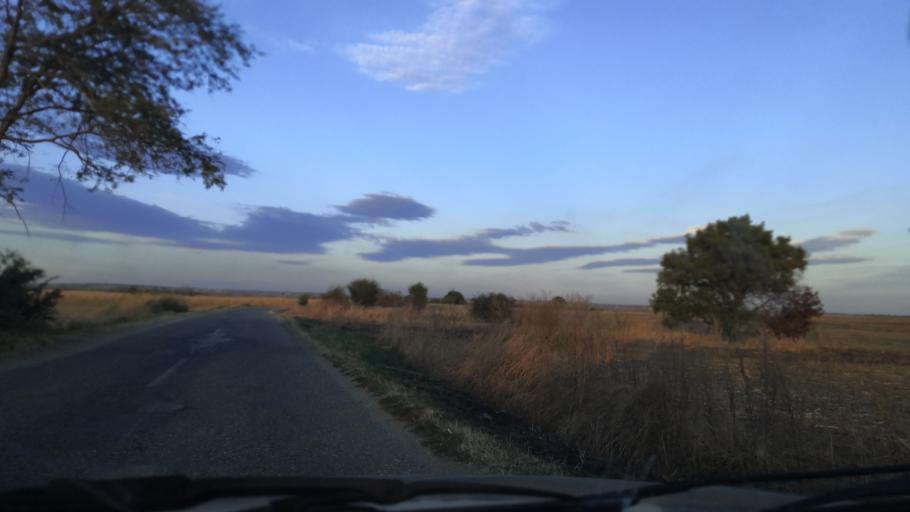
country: RO
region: Mehedinti
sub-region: Comuna Gruia
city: Izvoarele
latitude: 44.2618
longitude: 22.6406
